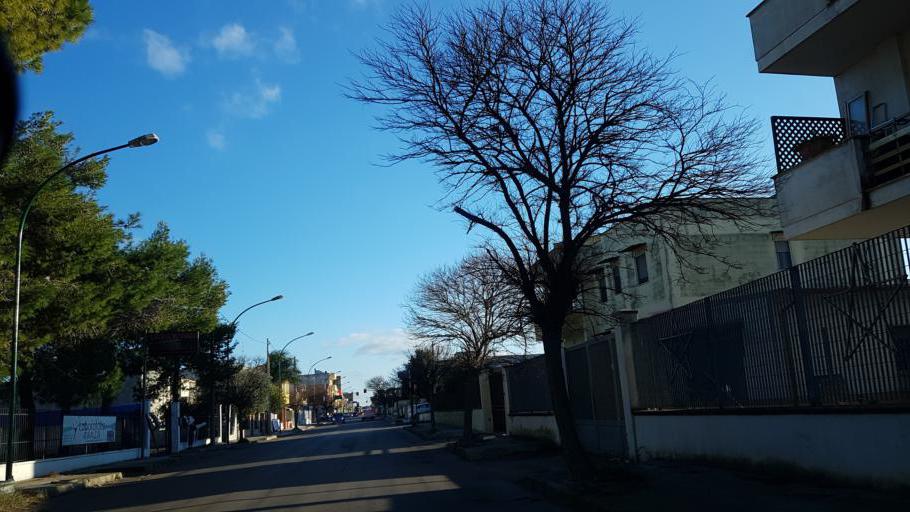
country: IT
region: Apulia
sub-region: Provincia di Lecce
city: Squinzano
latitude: 40.4430
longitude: 18.0344
